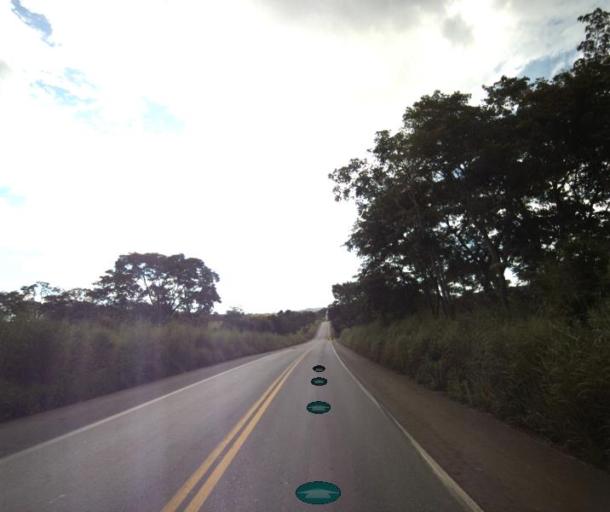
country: BR
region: Goias
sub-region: Jaragua
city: Jaragua
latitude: -15.6556
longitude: -49.3617
